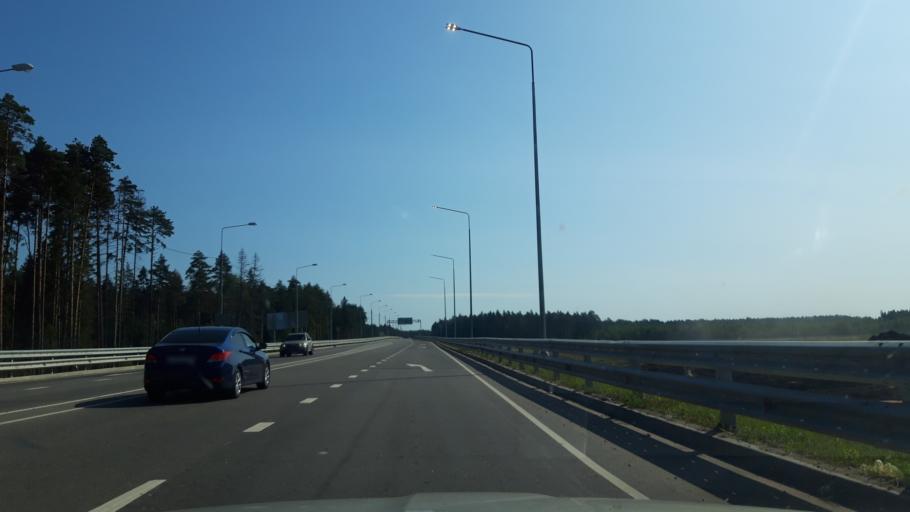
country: RU
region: Tverskaya
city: Novozavidovskiy
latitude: 56.5738
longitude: 36.4674
